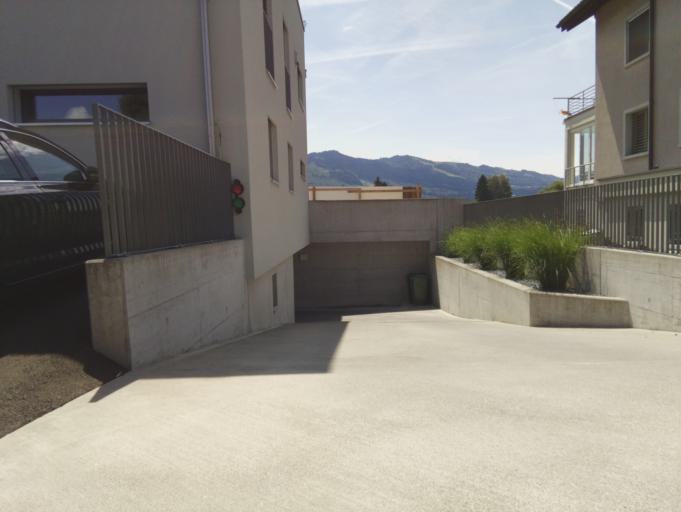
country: CH
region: Schwyz
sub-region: Bezirk March
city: Lachen
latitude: 47.1932
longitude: 8.8881
